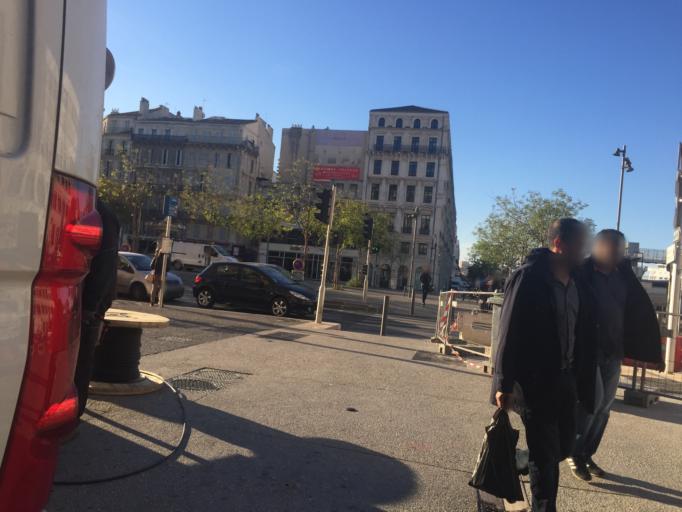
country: FR
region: Provence-Alpes-Cote d'Azur
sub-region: Departement des Bouches-du-Rhone
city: Marseille 02
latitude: 43.3054
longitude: 5.3655
